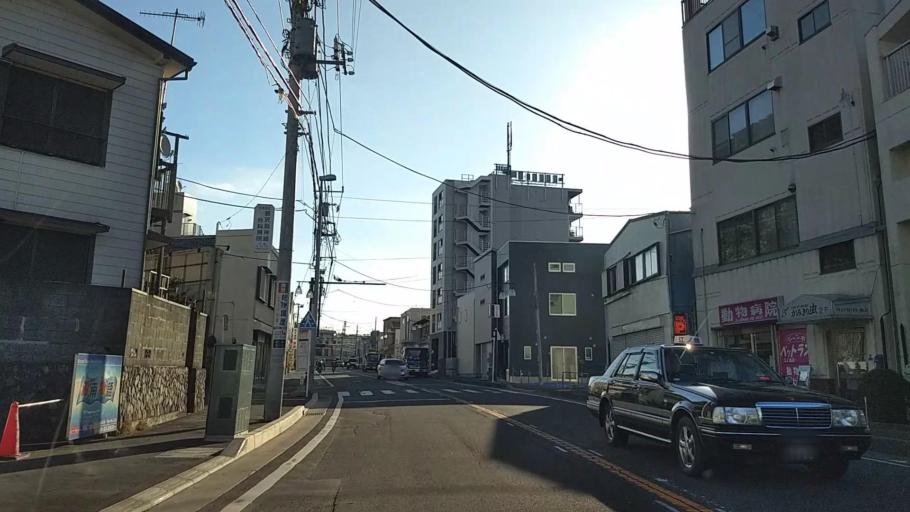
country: JP
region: Kanagawa
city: Fujisawa
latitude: 35.3114
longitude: 139.4875
